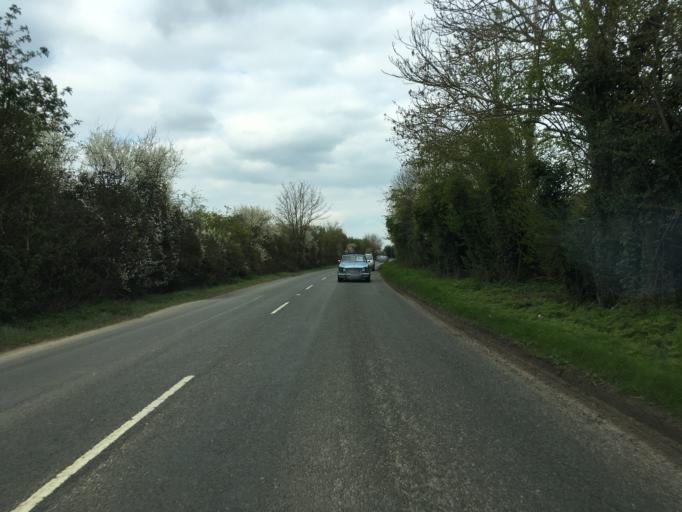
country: GB
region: England
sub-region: Oxfordshire
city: Bicester
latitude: 51.9058
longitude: -1.1766
